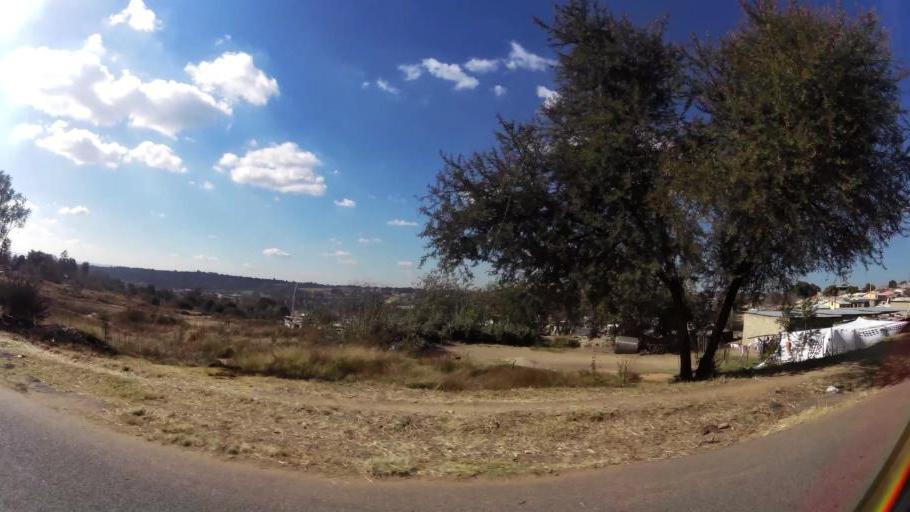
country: ZA
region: Gauteng
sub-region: West Rand District Municipality
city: Muldersdriseloop
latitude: -26.0492
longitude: 27.9062
